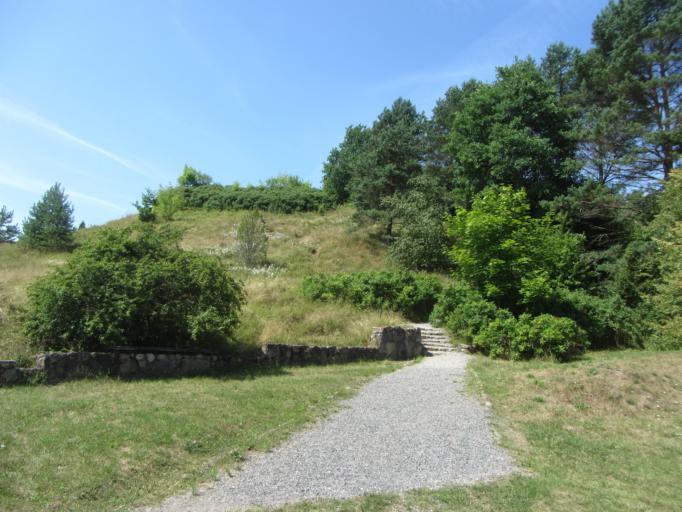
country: LT
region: Alytaus apskritis
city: Druskininkai
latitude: 54.0818
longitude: 24.0504
